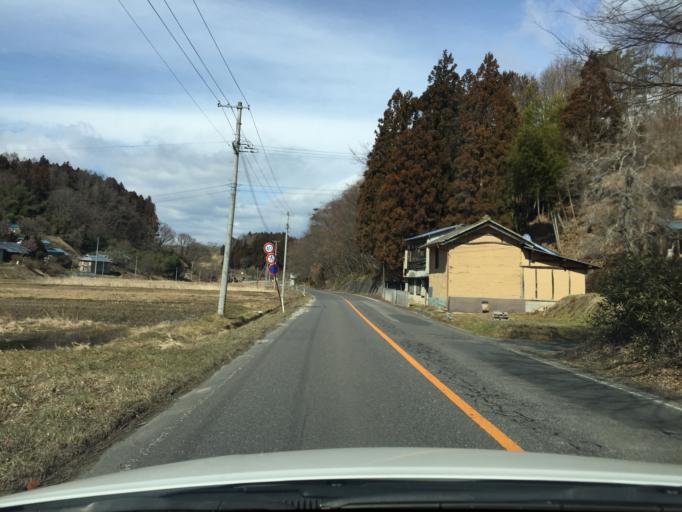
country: JP
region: Fukushima
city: Funehikimachi-funehiki
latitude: 37.4072
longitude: 140.5474
